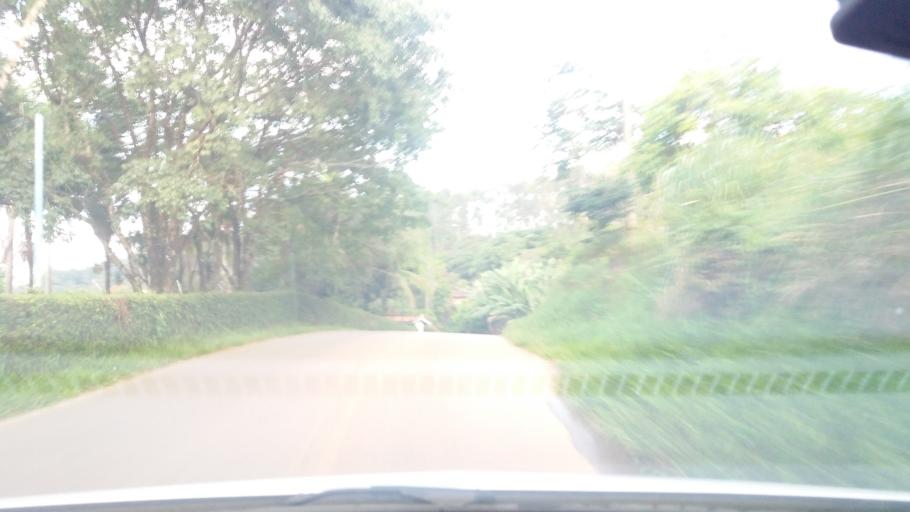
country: BR
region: Sao Paulo
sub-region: Bom Jesus Dos Perdoes
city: Bom Jesus dos Perdoes
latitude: -23.1737
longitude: -46.4818
